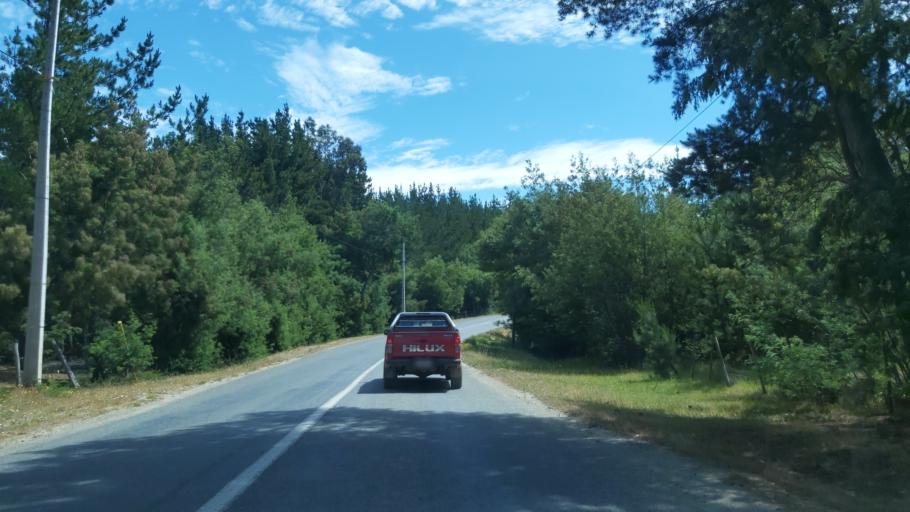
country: CL
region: Maule
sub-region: Provincia de Talca
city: Constitucion
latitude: -35.5507
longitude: -72.5689
